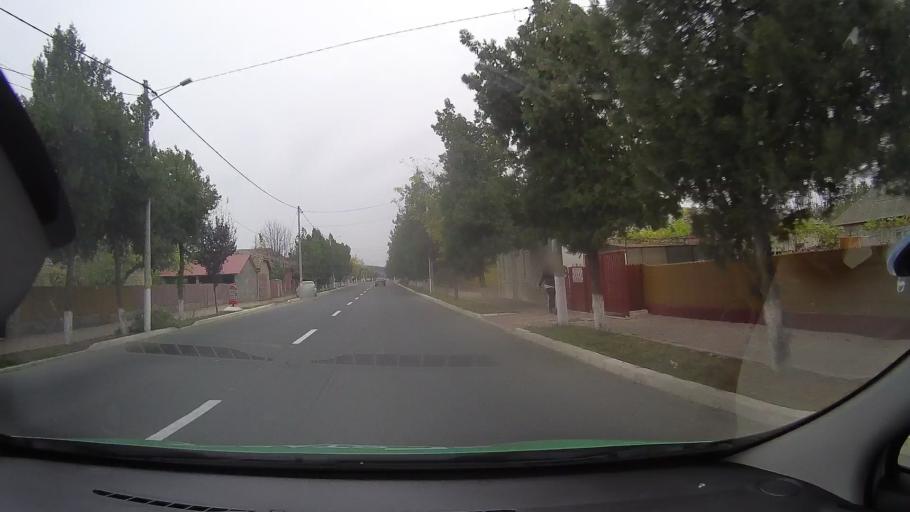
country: RO
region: Constanta
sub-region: Oras Harsova
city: Harsova
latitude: 44.6889
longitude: 27.9469
